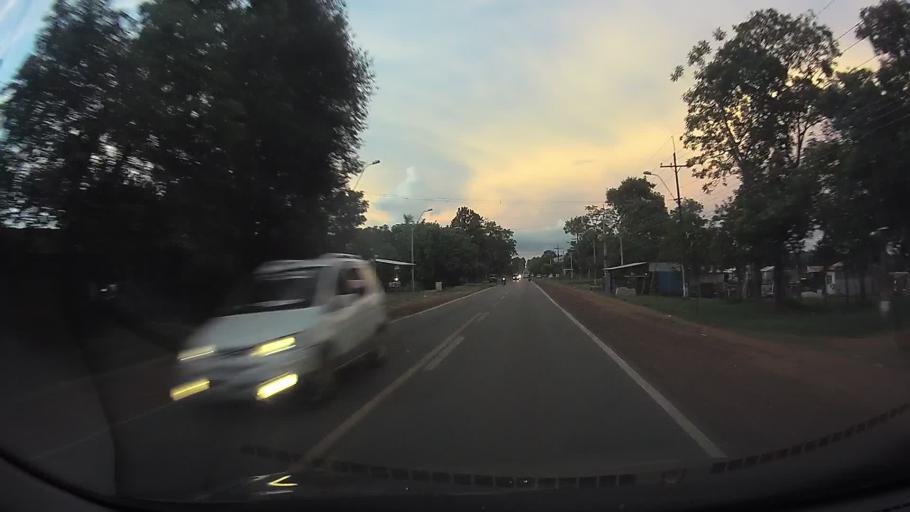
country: PY
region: Central
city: Ita
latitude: -25.4888
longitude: -57.3600
